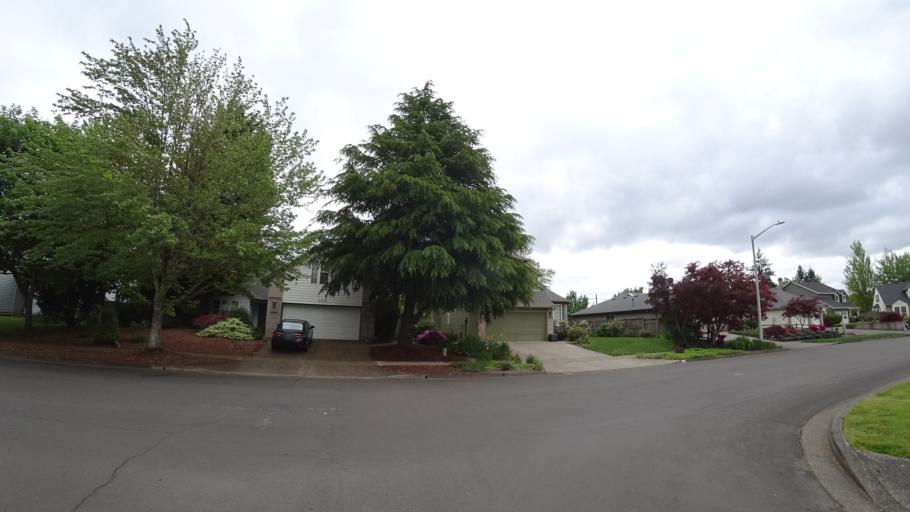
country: US
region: Oregon
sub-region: Washington County
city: Hillsboro
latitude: 45.5410
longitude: -122.9805
